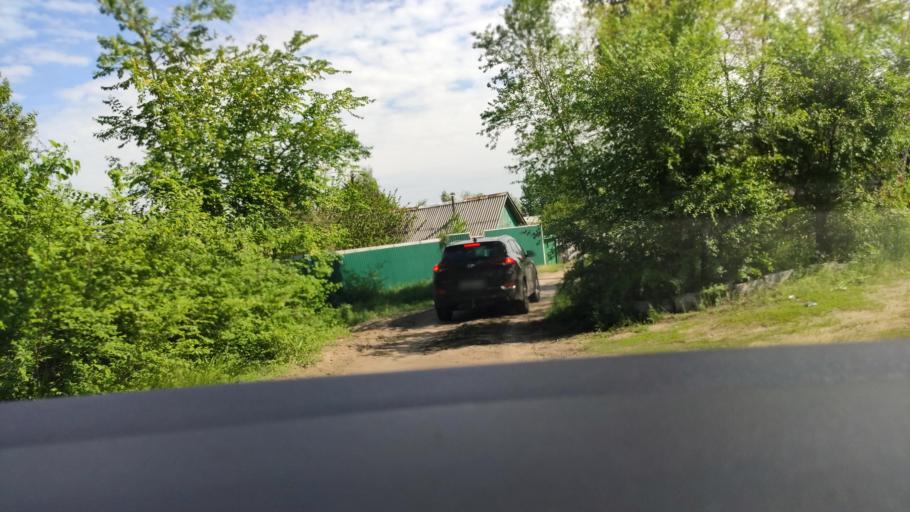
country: RU
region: Voronezj
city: Maslovka
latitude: 51.6146
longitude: 39.2286
